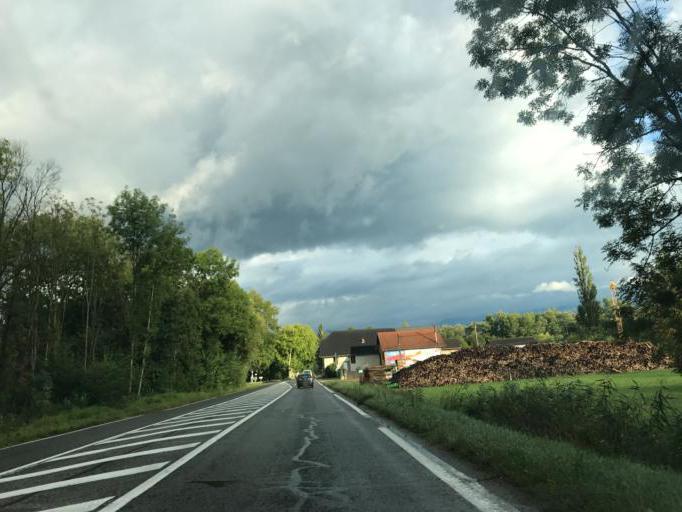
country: FR
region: Rhone-Alpes
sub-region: Departement de la Savoie
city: Les Marches
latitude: 45.5115
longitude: 6.0125
